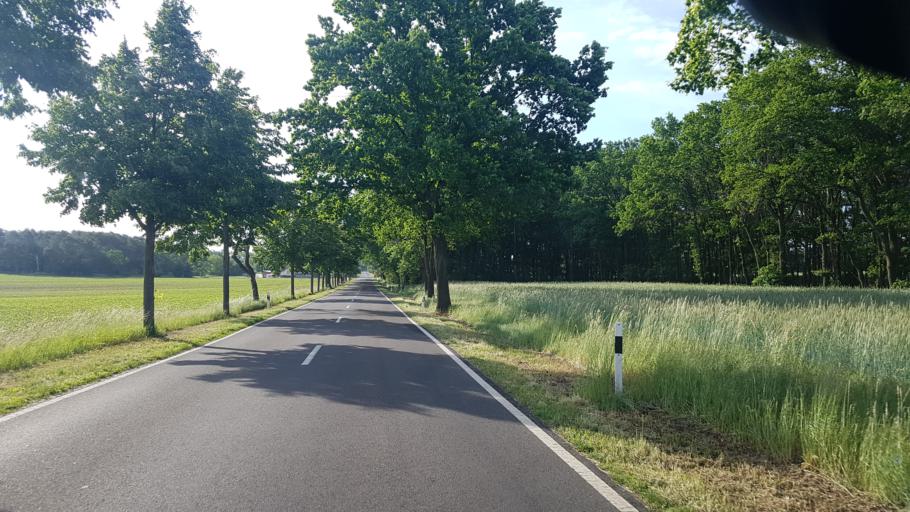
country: DE
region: Brandenburg
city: Luckau
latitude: 51.8238
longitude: 13.6852
